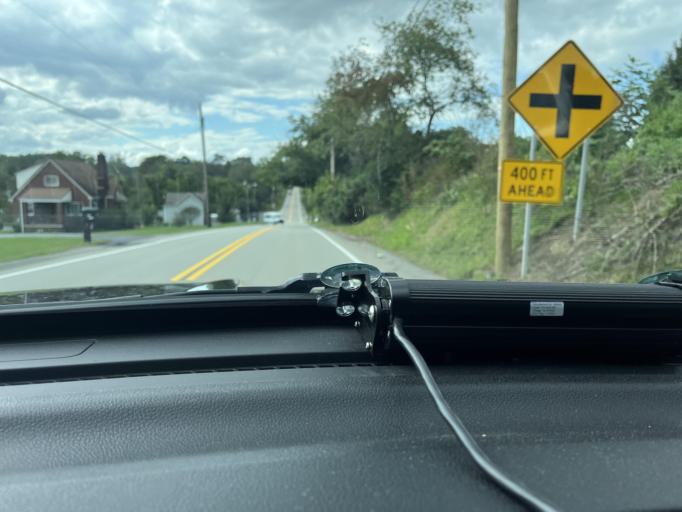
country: US
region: Pennsylvania
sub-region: Fayette County
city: South Uniontown
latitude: 39.9094
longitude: -79.7677
